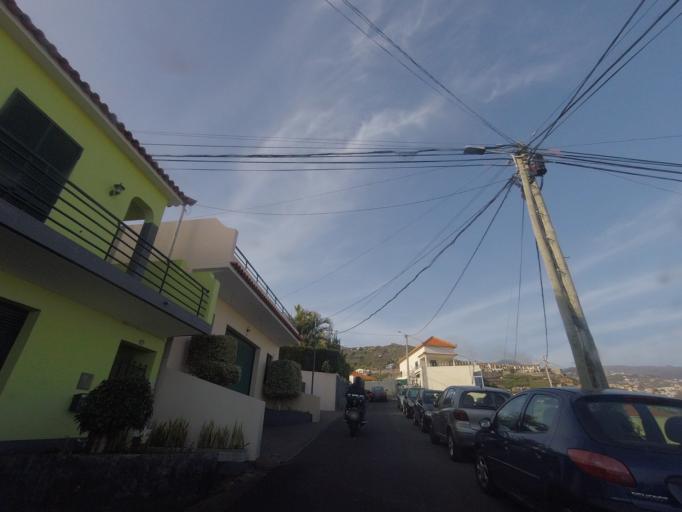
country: PT
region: Madeira
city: Camara de Lobos
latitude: 32.6538
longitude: -16.9893
